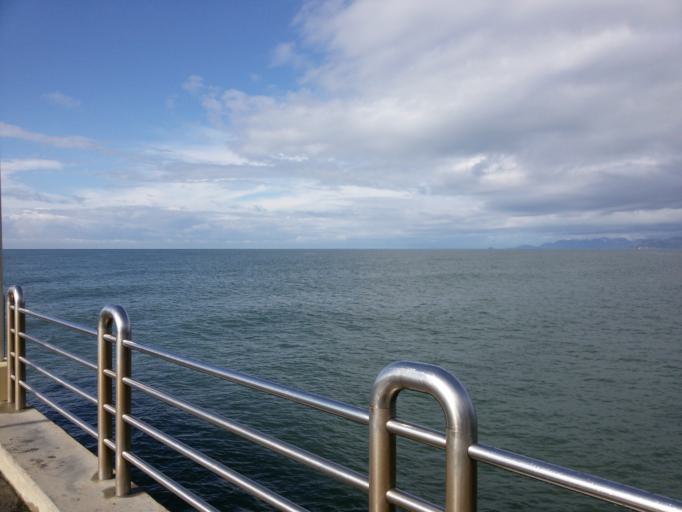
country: IT
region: Tuscany
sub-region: Provincia di Lucca
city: Forte dei Marmi
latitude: 43.9558
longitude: 10.1637
